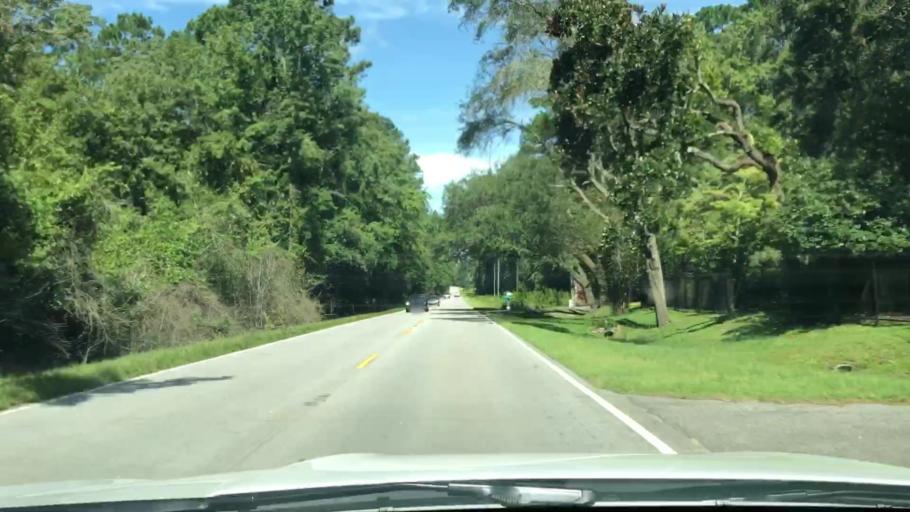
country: US
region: South Carolina
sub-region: Dorchester County
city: Centerville
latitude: 32.9419
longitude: -80.1885
